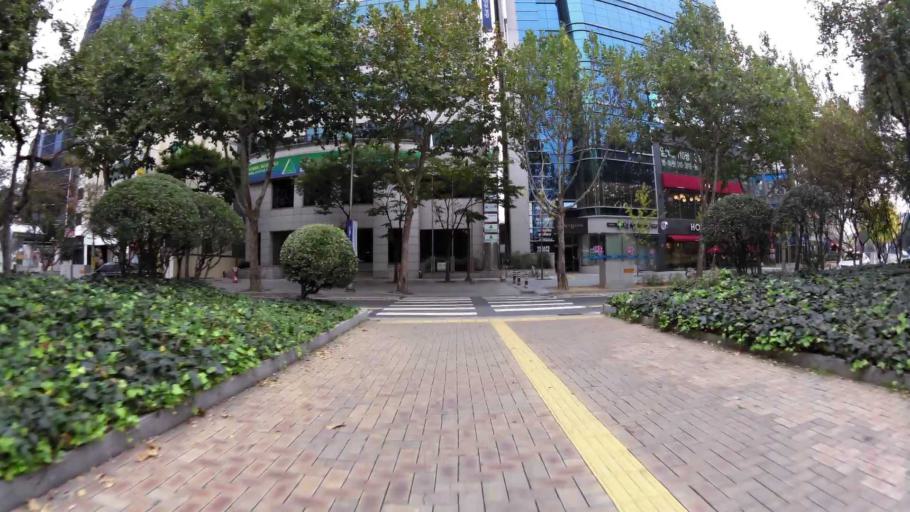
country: KR
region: Daegu
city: Daegu
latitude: 35.8586
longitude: 128.6267
